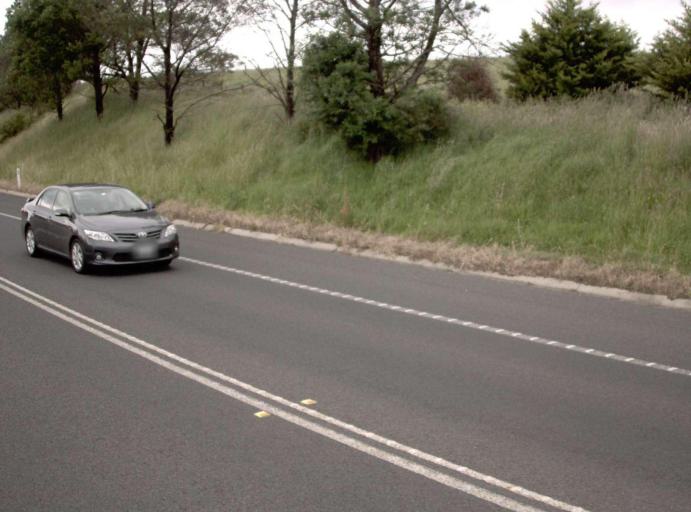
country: AU
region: Victoria
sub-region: Baw Baw
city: Warragul
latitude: -38.4473
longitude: 145.8926
